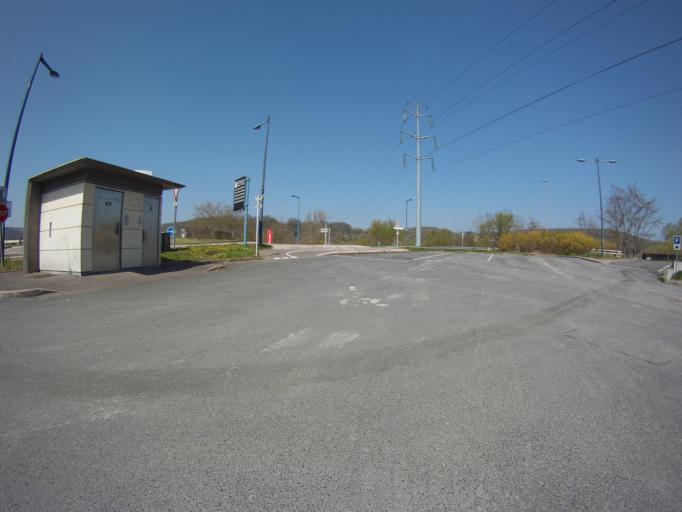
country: FR
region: Lorraine
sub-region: Departement de Meurthe-et-Moselle
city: Custines
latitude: 48.7879
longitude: 6.1389
